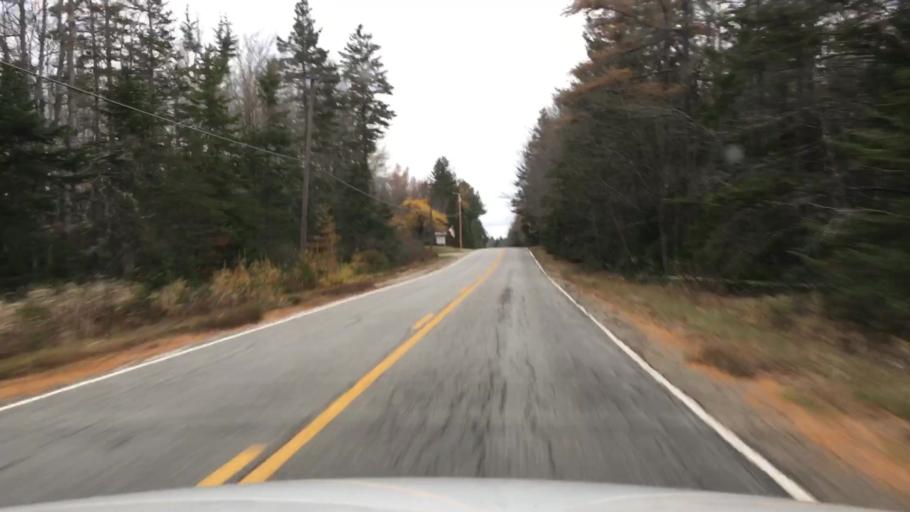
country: US
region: Maine
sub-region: Hancock County
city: Sedgwick
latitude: 44.2816
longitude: -68.5541
